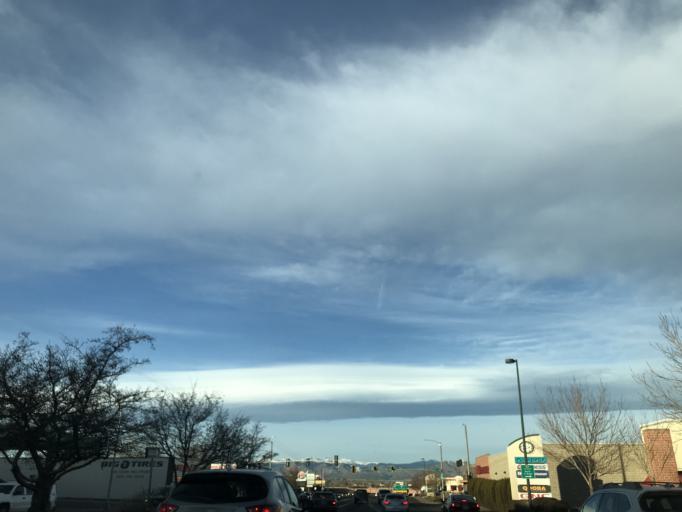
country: US
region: Colorado
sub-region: Arapahoe County
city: Englewood
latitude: 39.6533
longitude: -104.9968
